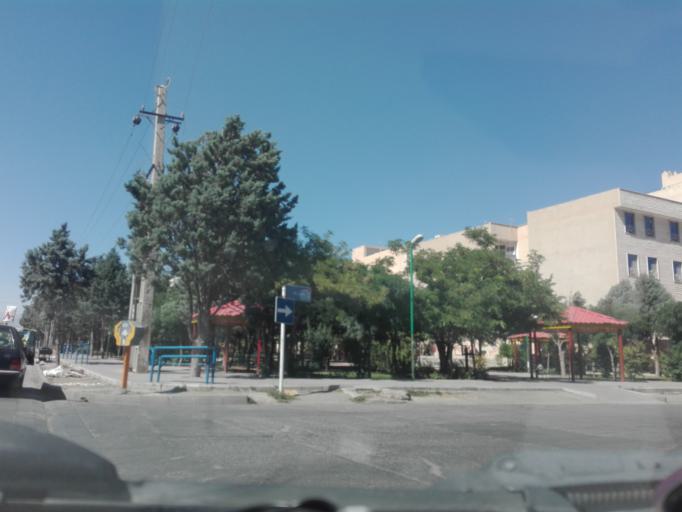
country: IR
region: Tehran
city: Shahre Jadide Andisheh
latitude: 35.7216
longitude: 50.9839
